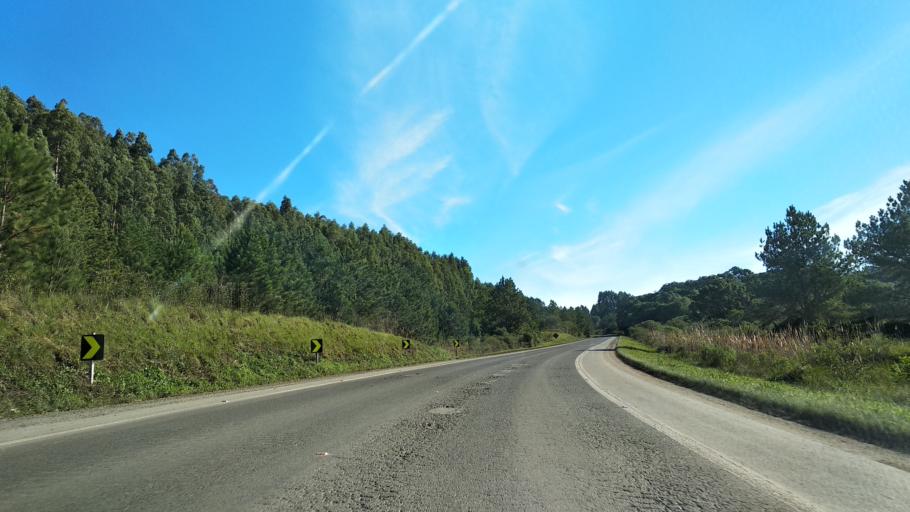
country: BR
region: Santa Catarina
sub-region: Campos Novos
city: Campos Novos
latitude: -27.3993
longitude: -51.1958
